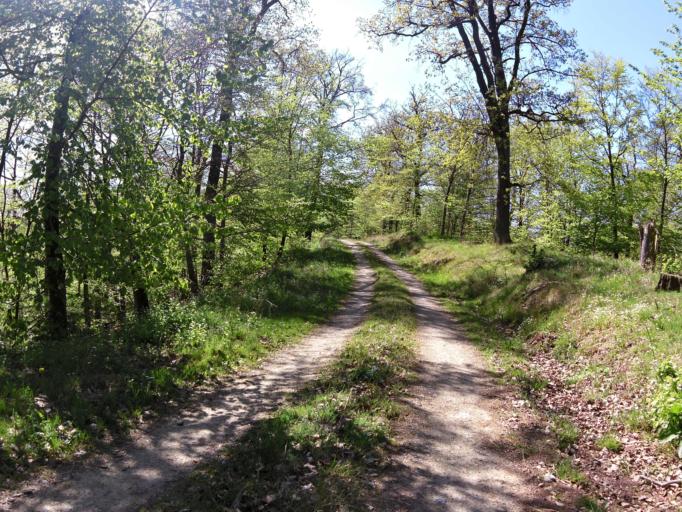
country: DE
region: Thuringia
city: Wolfsburg-Unkeroda
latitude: 50.9633
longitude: 10.2648
